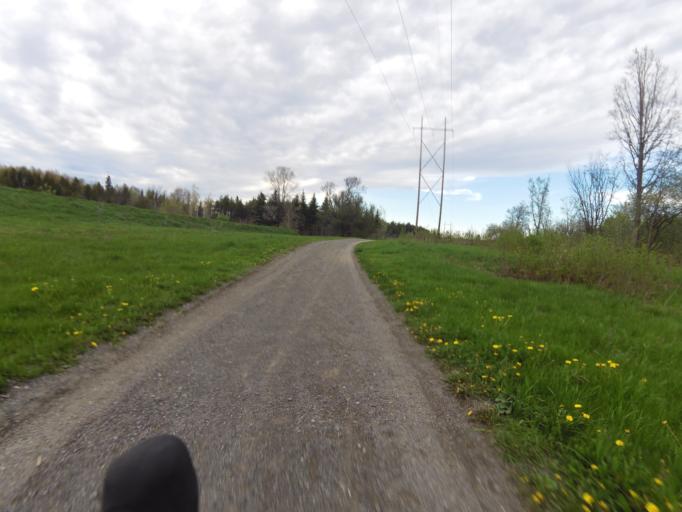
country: CA
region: Ontario
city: Bells Corners
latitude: 45.2919
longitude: -75.7982
